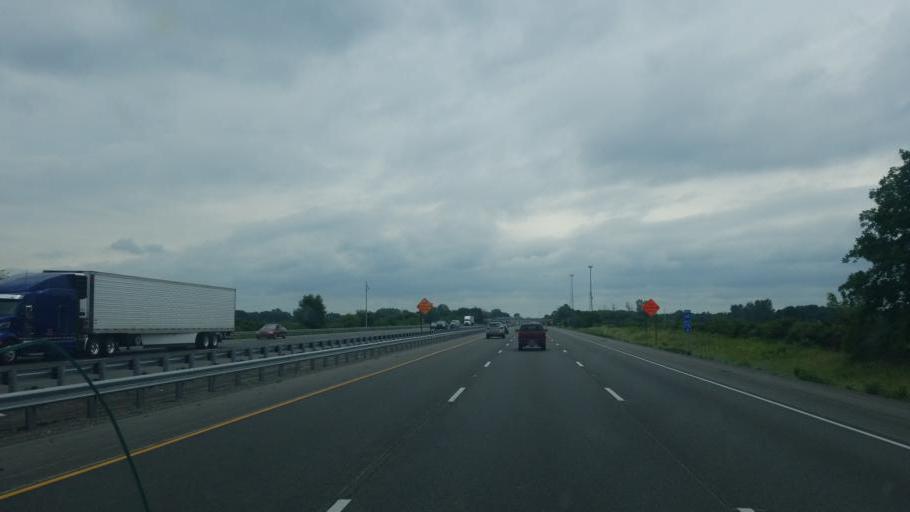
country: US
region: Indiana
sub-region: Madison County
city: Ingalls
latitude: 39.9915
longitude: -85.8036
